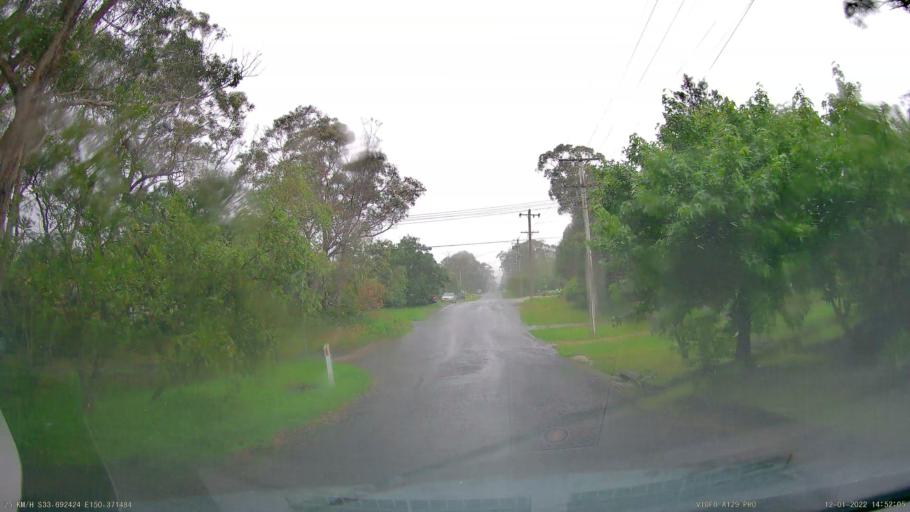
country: AU
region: New South Wales
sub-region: Blue Mountains Municipality
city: Leura
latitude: -33.6925
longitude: 150.3715
